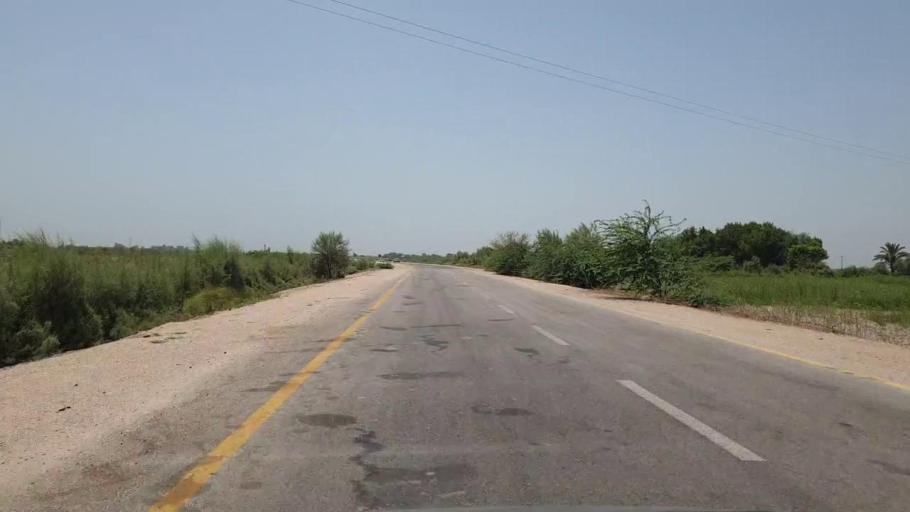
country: PK
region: Sindh
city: Sakrand
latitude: 26.1296
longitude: 68.3775
